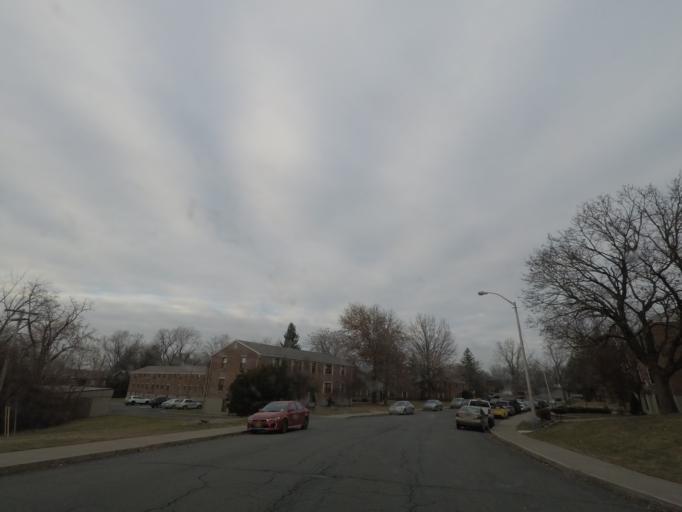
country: US
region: New York
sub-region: Albany County
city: Green Island
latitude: 42.7393
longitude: -73.6697
